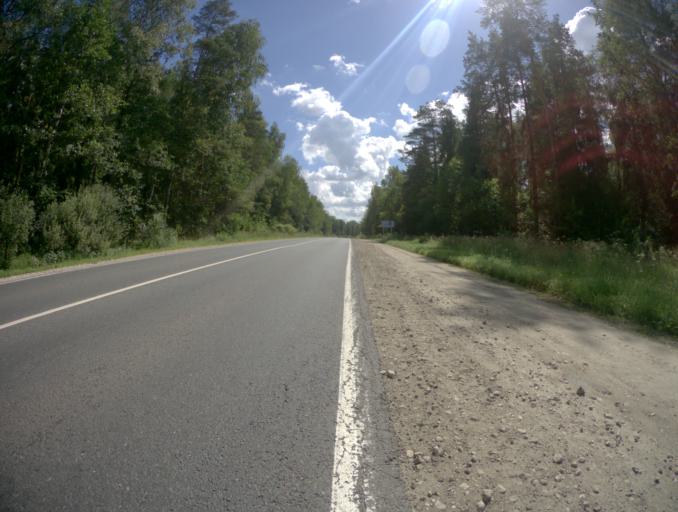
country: RU
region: Vladimir
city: Kommunar
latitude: 56.0183
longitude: 40.5828
